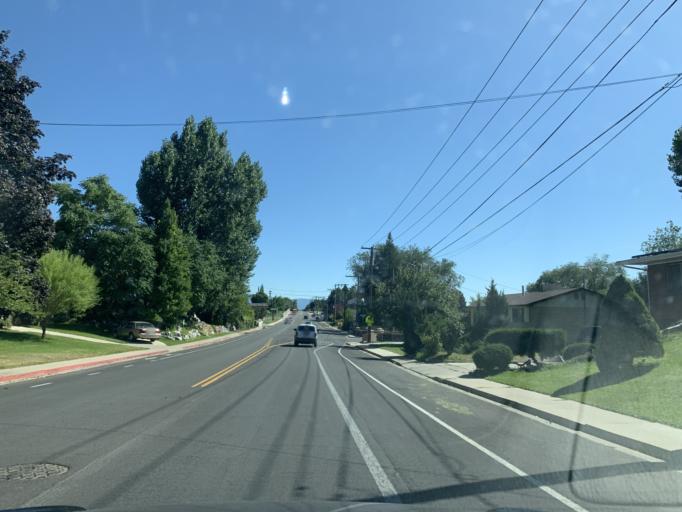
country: US
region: Utah
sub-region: Utah County
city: Orem
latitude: 40.2819
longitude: -111.7049
